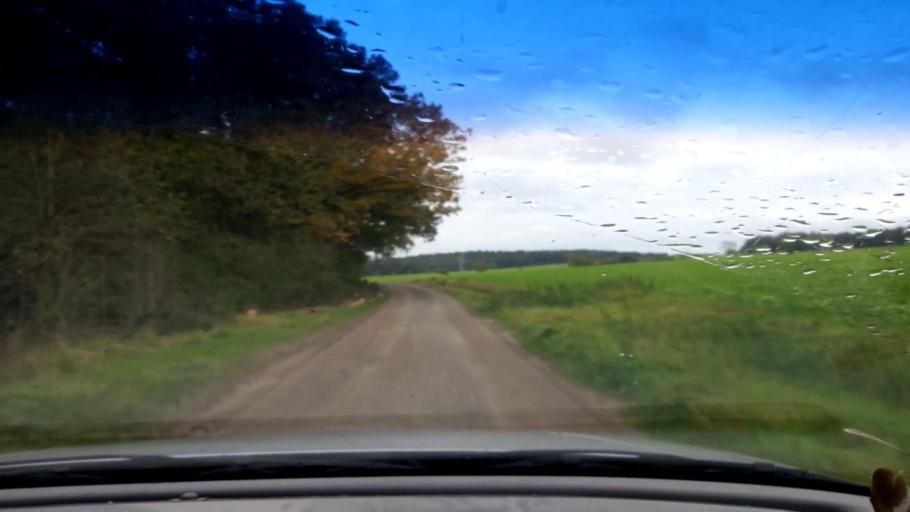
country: DE
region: Bavaria
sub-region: Regierungsbezirk Unterfranken
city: Kirchlauter
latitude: 50.0346
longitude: 10.7381
